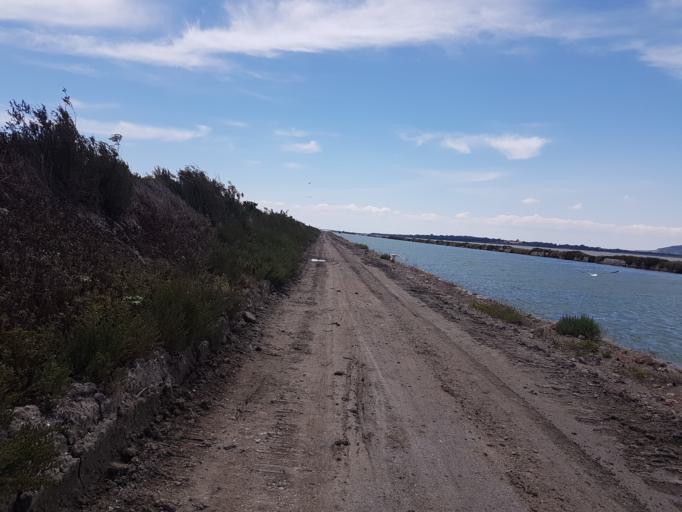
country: FR
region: Languedoc-Roussillon
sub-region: Departement de l'Herault
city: Vic-la-Gardiole
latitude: 43.4818
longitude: 3.8367
